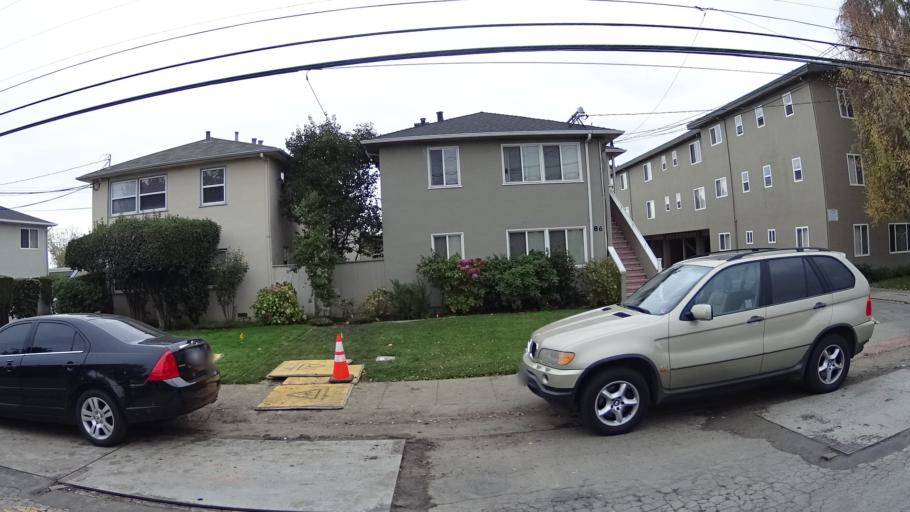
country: US
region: California
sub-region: San Mateo County
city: Belmont
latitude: 37.5351
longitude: -122.2898
